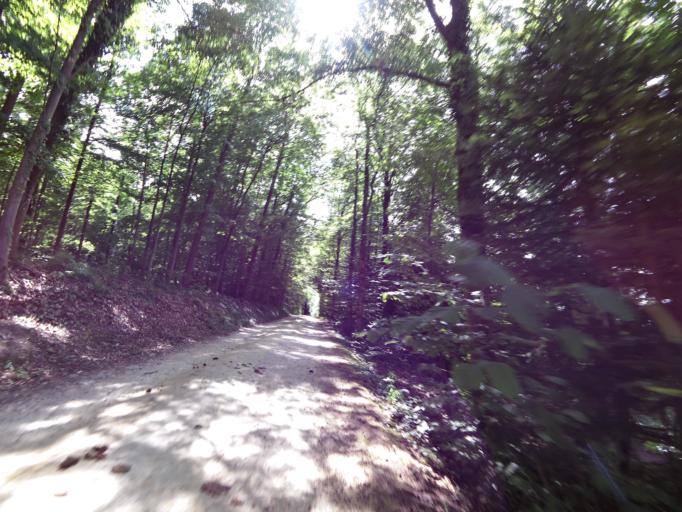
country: CH
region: Aargau
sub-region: Bezirk Rheinfelden
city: Mohlin
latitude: 47.5823
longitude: 7.8536
